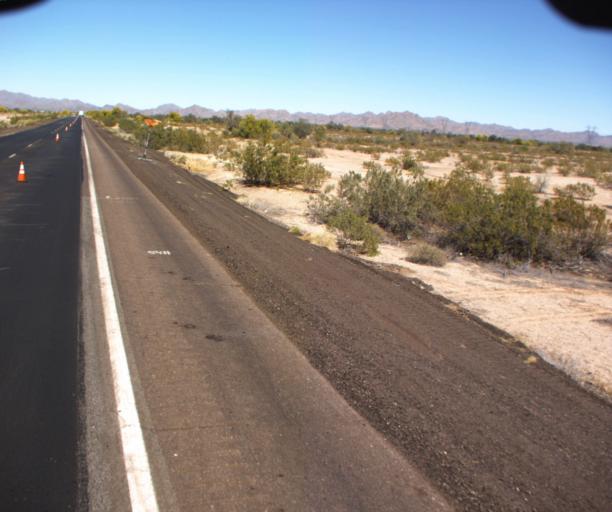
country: US
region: Arizona
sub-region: Maricopa County
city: Gila Bend
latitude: 33.0073
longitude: -112.6556
